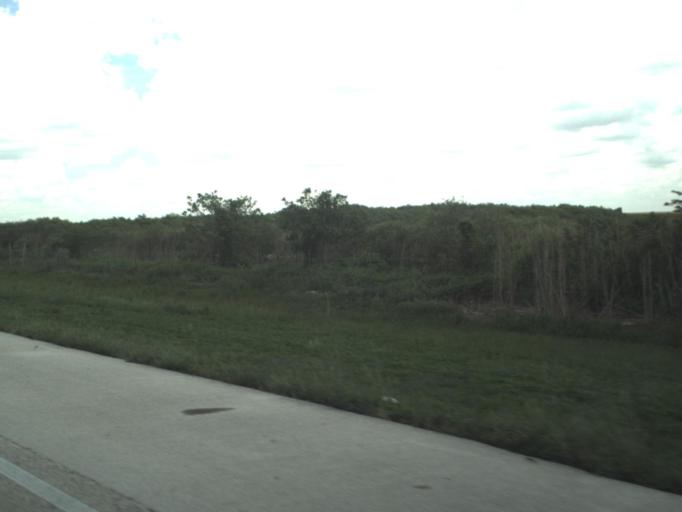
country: US
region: Florida
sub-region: Broward County
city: Weston
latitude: 26.1465
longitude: -80.5842
